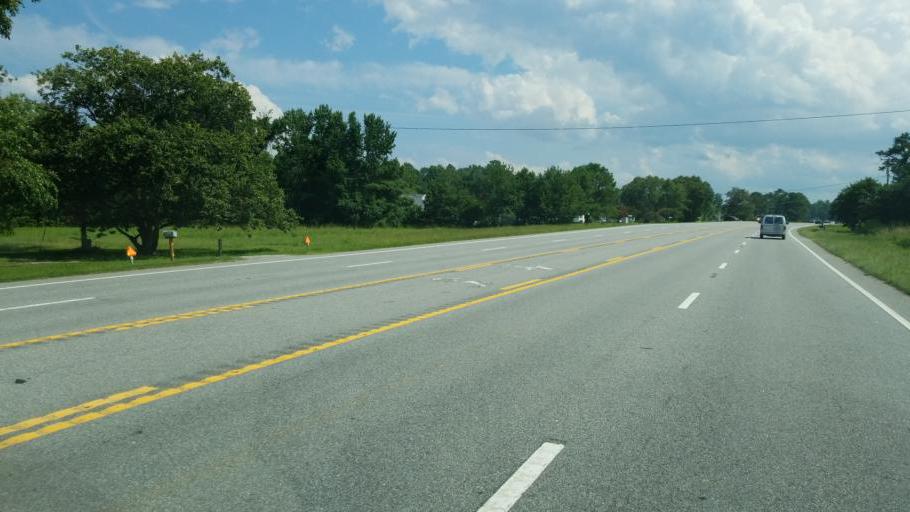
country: US
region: North Carolina
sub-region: Currituck County
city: Currituck
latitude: 36.4302
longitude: -76.0072
